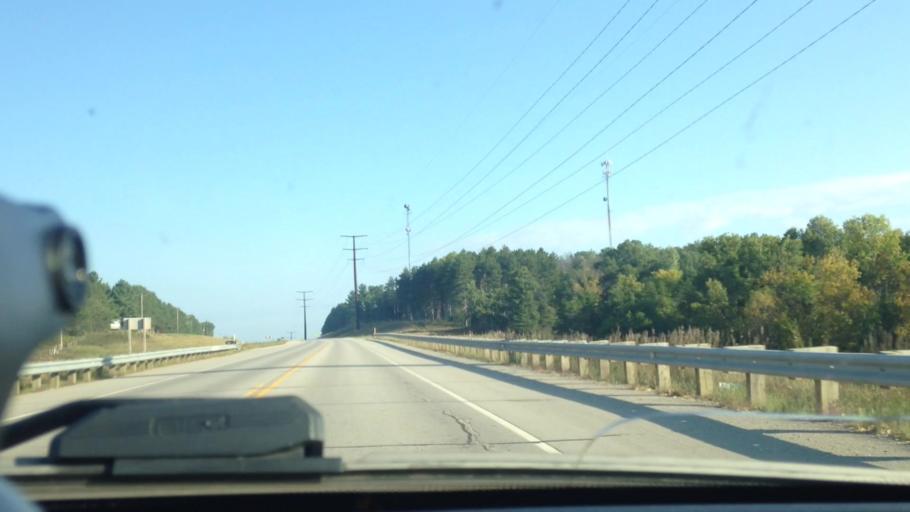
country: US
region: Wisconsin
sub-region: Marinette County
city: Peshtigo
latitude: 45.2093
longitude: -87.9946
